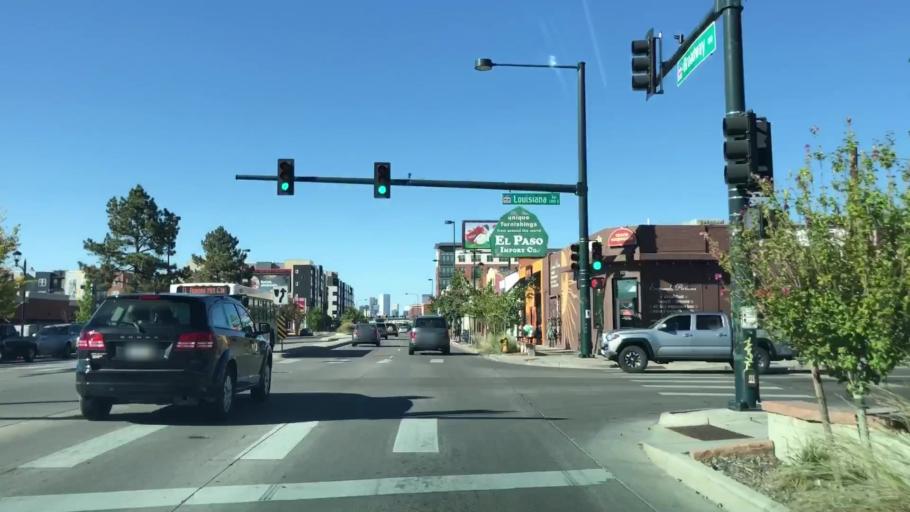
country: US
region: Colorado
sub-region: Arapahoe County
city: Englewood
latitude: 39.6928
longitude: -104.9874
